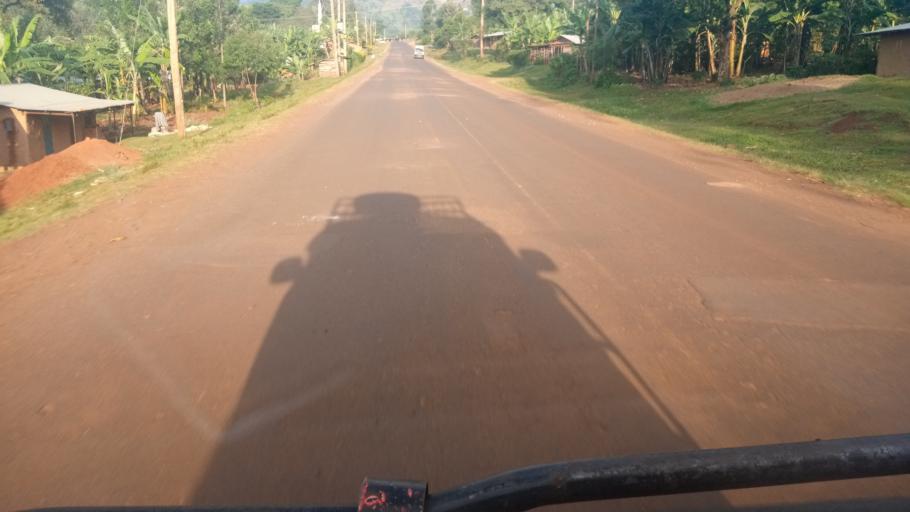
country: UG
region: Eastern Region
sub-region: Kapchorwa District
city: Kapchorwa
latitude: 1.3229
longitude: 34.3469
